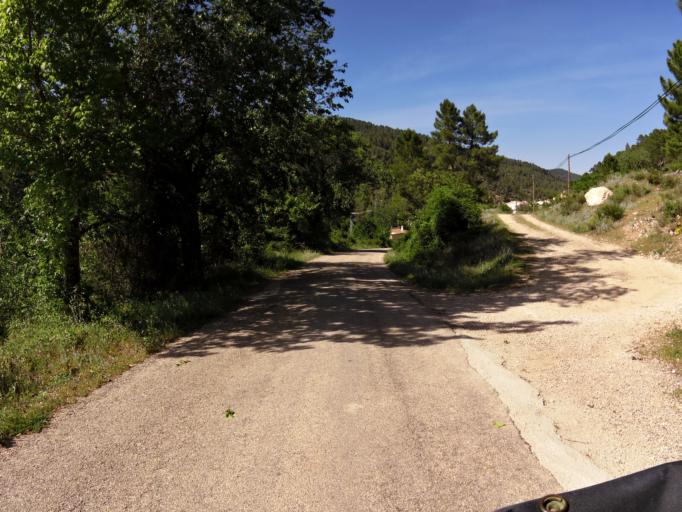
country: ES
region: Castille-La Mancha
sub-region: Provincia de Albacete
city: Paterna del Madera
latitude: 38.5874
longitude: -2.3114
